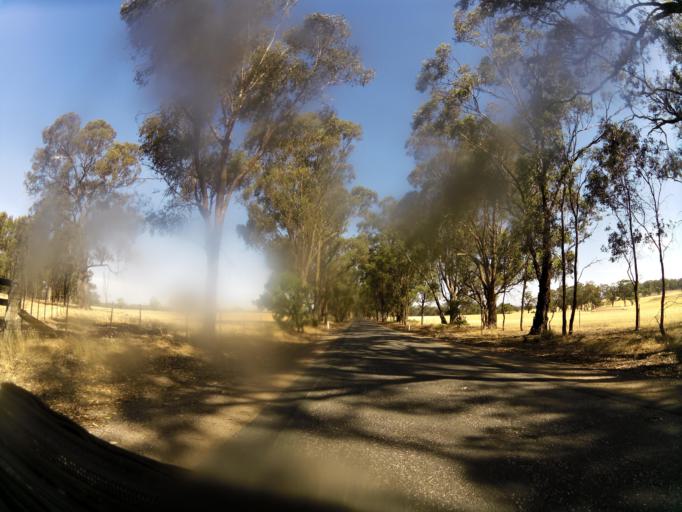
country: AU
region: Victoria
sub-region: Campaspe
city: Kyabram
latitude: -36.8890
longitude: 145.1028
